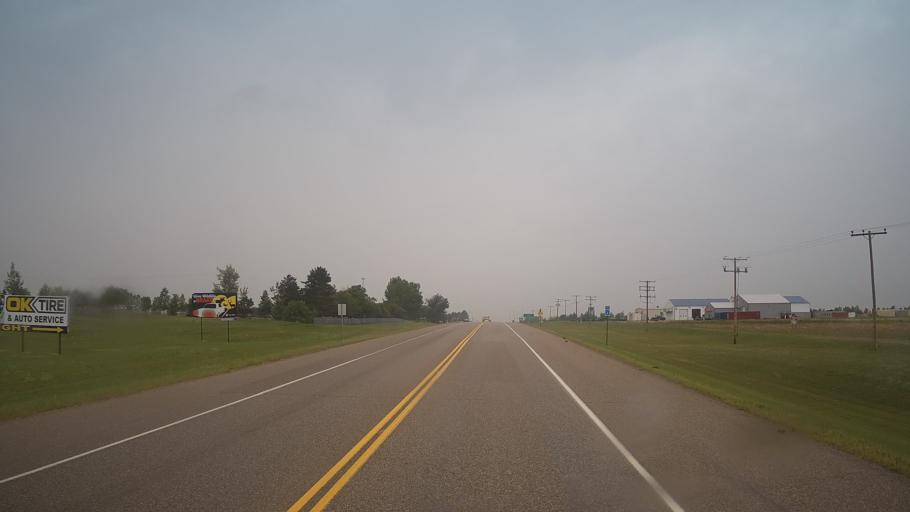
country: CA
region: Saskatchewan
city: Biggar
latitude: 52.0607
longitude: -107.9714
